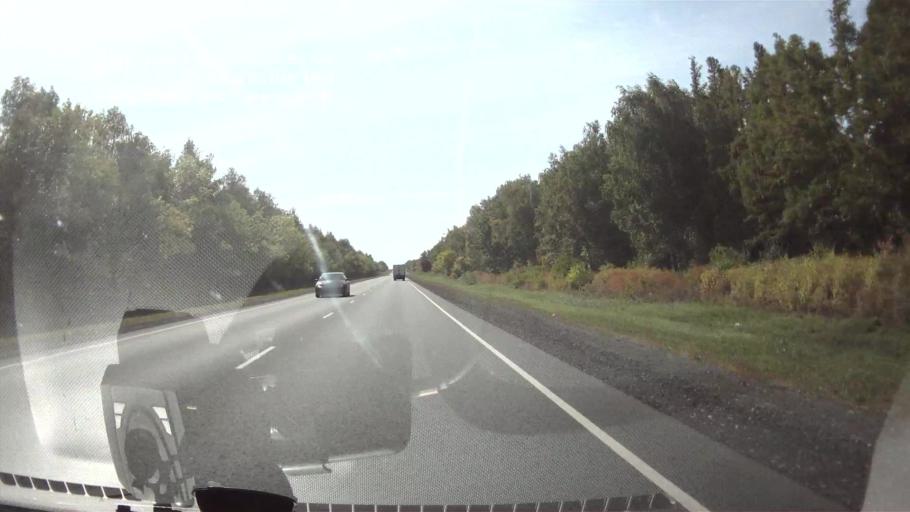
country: RU
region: Saratov
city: Khvalynsk
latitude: 52.5725
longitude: 48.1046
